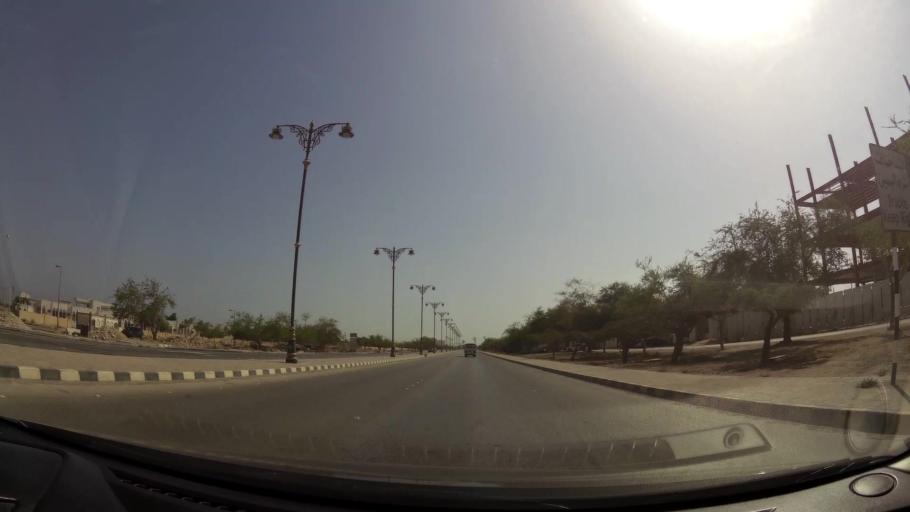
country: OM
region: Zufar
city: Salalah
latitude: 17.0134
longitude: 54.0510
